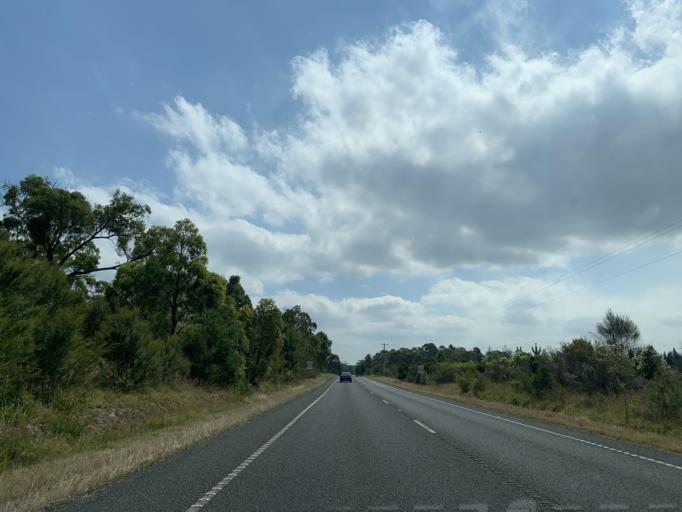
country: AU
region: Victoria
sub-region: Latrobe
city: Traralgon
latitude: -38.2027
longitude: 146.4671
